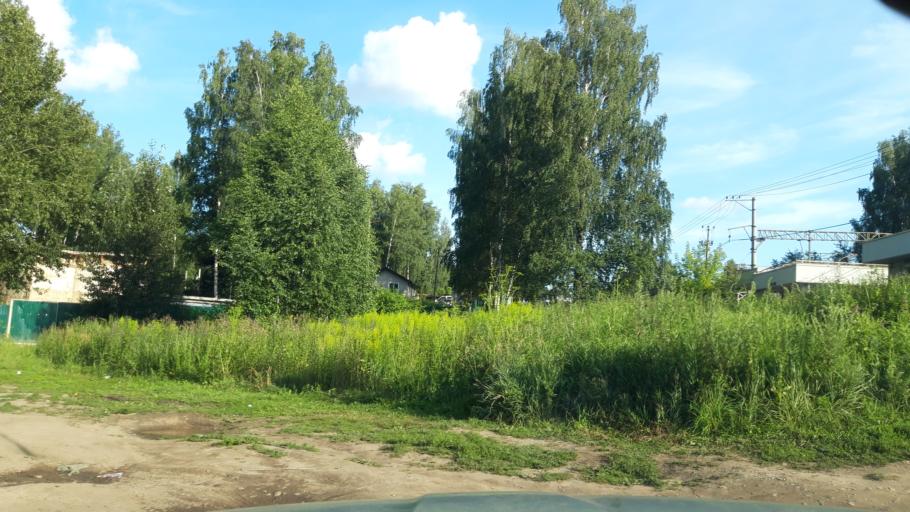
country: RU
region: Moskovskaya
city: Povarovo
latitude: 56.0650
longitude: 37.0761
